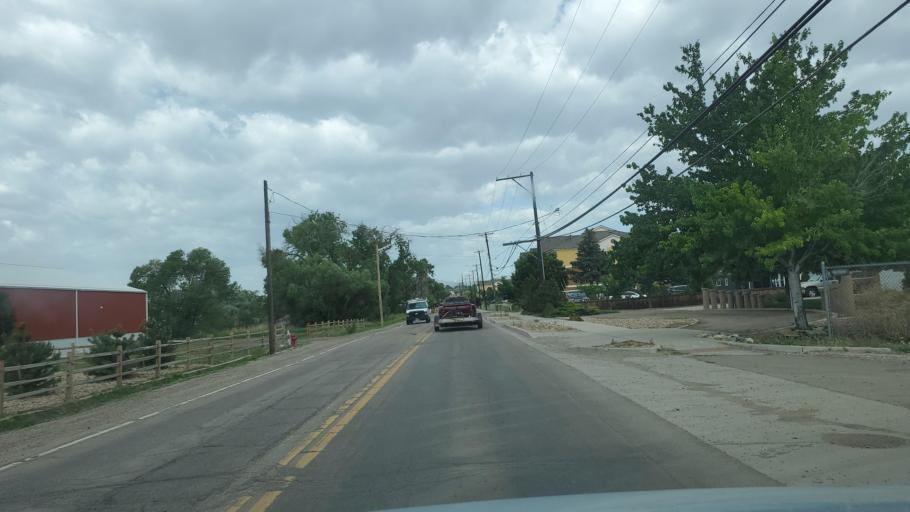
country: US
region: Colorado
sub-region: Adams County
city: Welby
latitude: 39.8381
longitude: -104.9618
